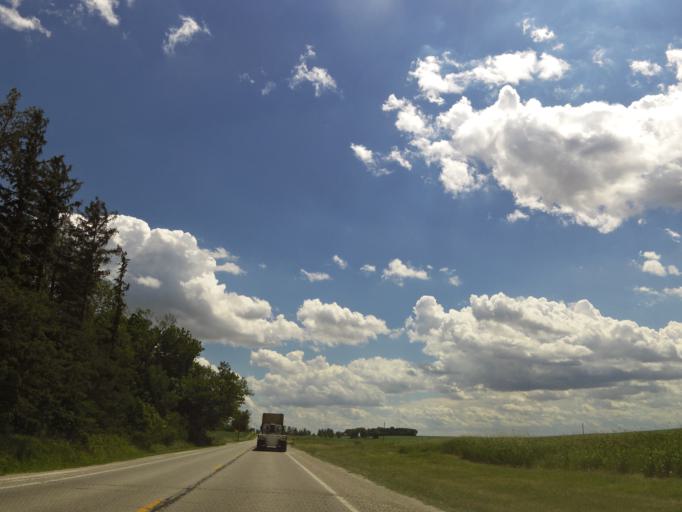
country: US
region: Iowa
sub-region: Buchanan County
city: Independence
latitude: 42.3506
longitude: -91.8892
